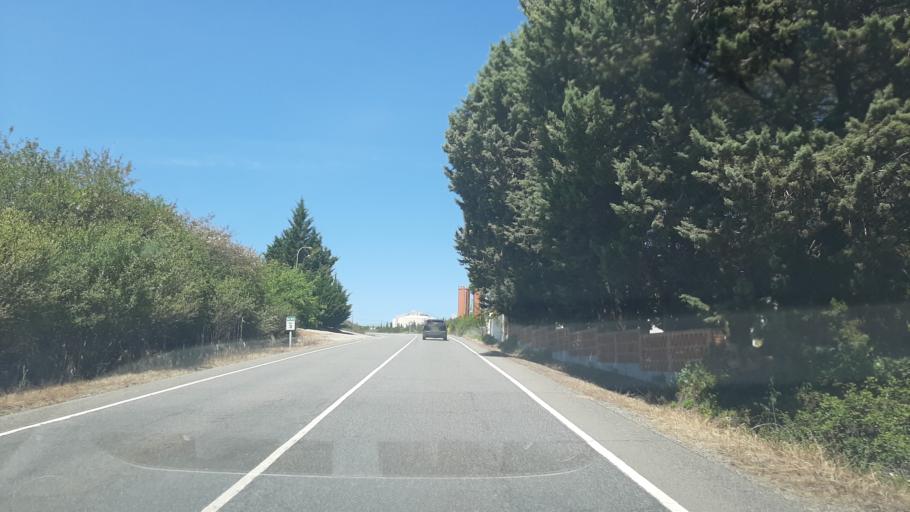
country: ES
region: Castille and Leon
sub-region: Provincia de Salamanca
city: Guijo de Avila
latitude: 40.5548
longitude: -5.6399
